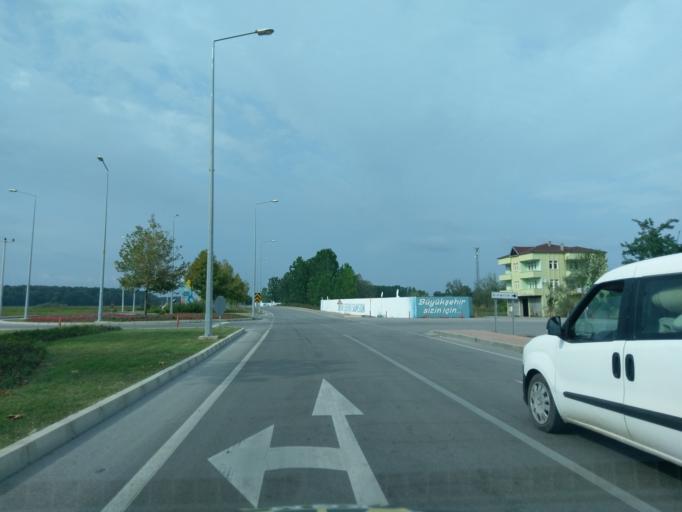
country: TR
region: Samsun
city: Dikbiyik
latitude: 41.2423
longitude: 36.5399
